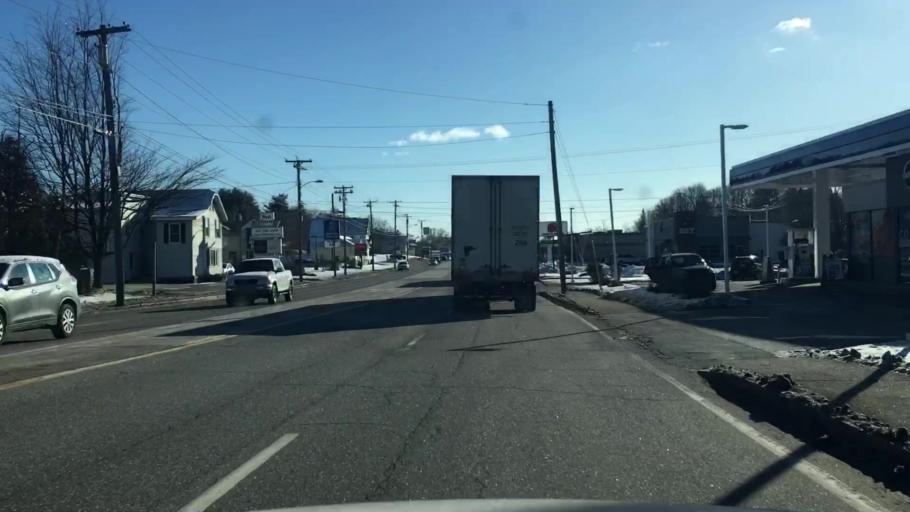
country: US
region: Maine
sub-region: Androscoggin County
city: Lewiston
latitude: 44.1188
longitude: -70.2253
